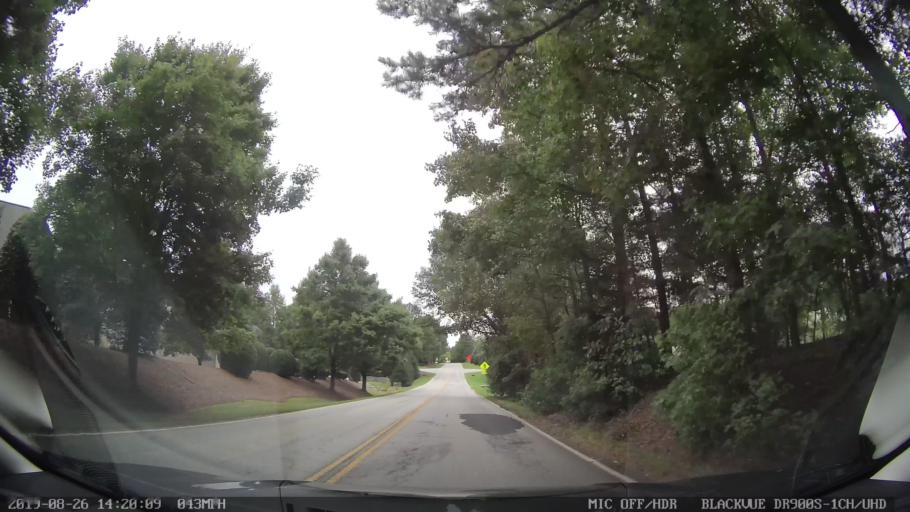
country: US
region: South Carolina
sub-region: Greenville County
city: Five Forks
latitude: 34.8004
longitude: -82.2483
